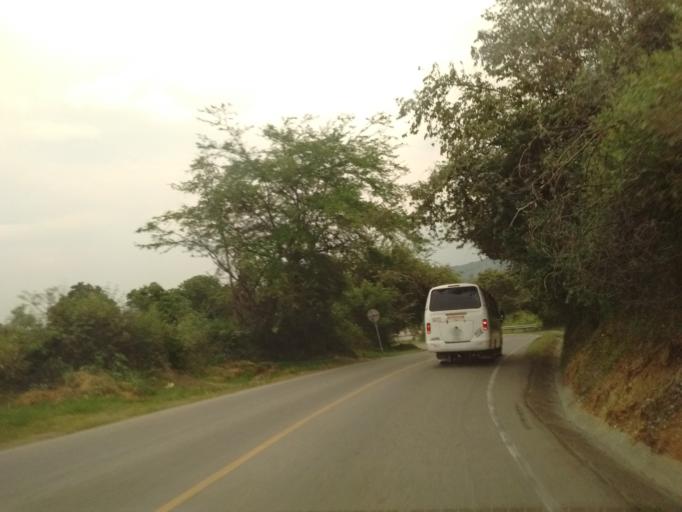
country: CO
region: Cauca
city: Caloto
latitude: 3.0637
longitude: -76.3668
